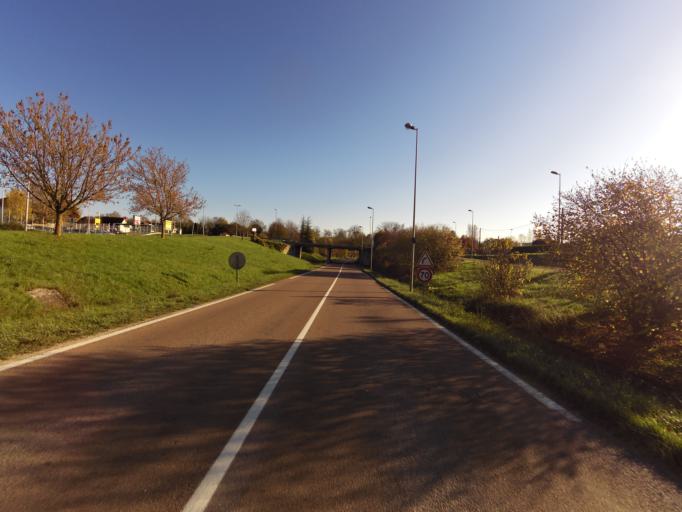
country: FR
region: Champagne-Ardenne
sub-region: Departement de l'Aube
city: Breviandes
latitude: 48.2607
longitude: 4.0916
